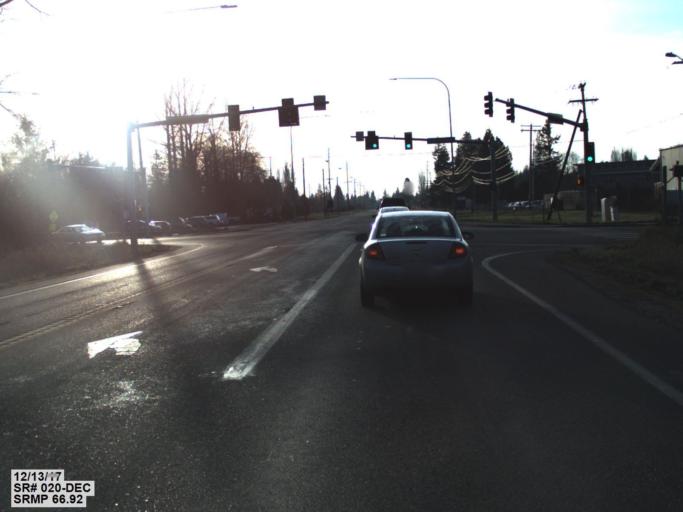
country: US
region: Washington
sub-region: Skagit County
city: Sedro-Woolley
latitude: 48.5162
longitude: -122.2098
